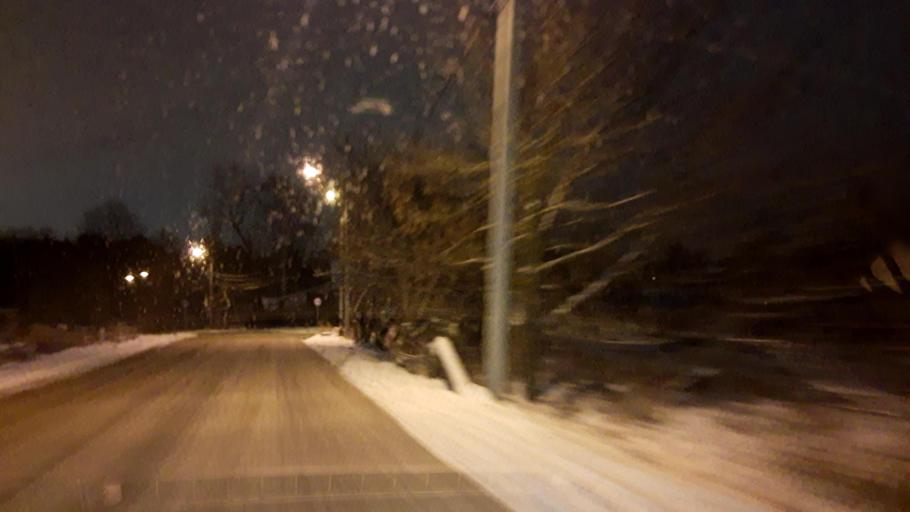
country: RU
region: Moskovskaya
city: Biryulevo Zapadnoye
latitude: 55.5696
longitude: 37.6233
